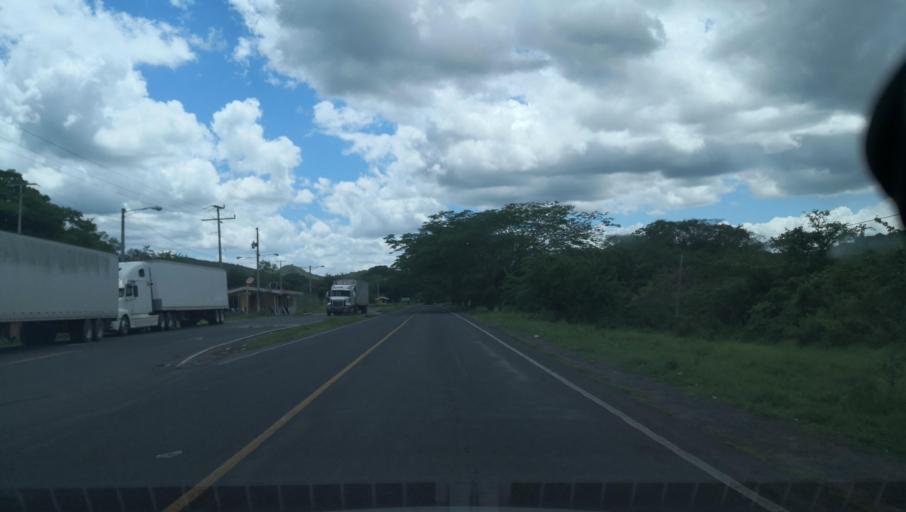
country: NI
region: Madriz
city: Palacaguina
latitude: 13.4330
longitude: -86.4117
